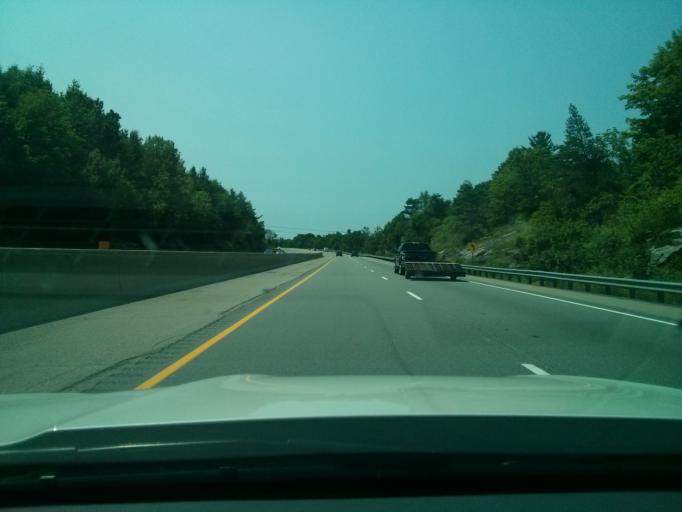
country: CA
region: Ontario
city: Brockville
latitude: 44.5830
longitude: -75.7305
